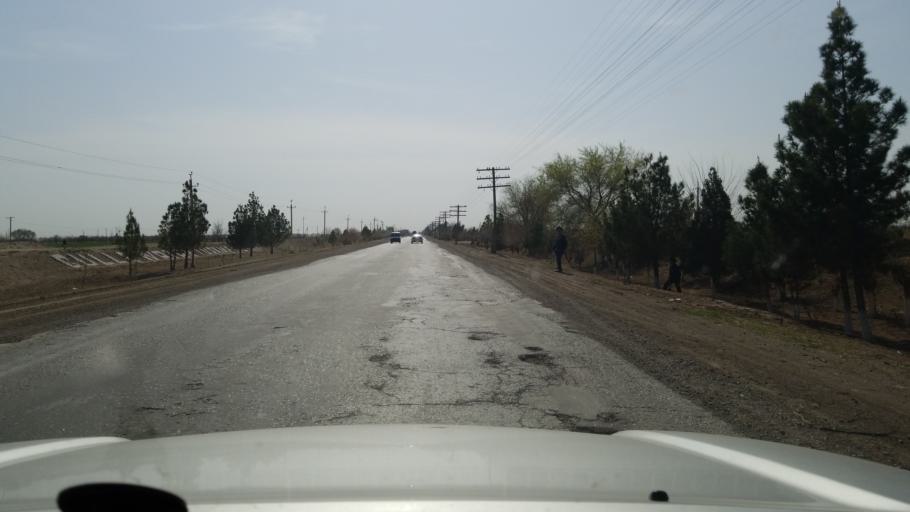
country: TM
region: Lebap
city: Sayat
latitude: 38.8139
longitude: 63.8370
